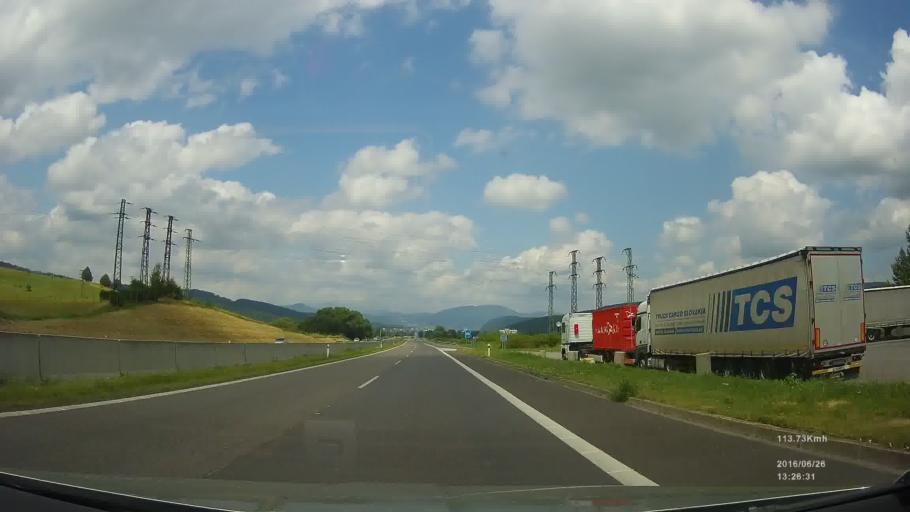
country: SK
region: Banskobystricky
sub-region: Okres Banska Bystrica
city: Banska Bystrica
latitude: 48.6675
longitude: 19.1331
